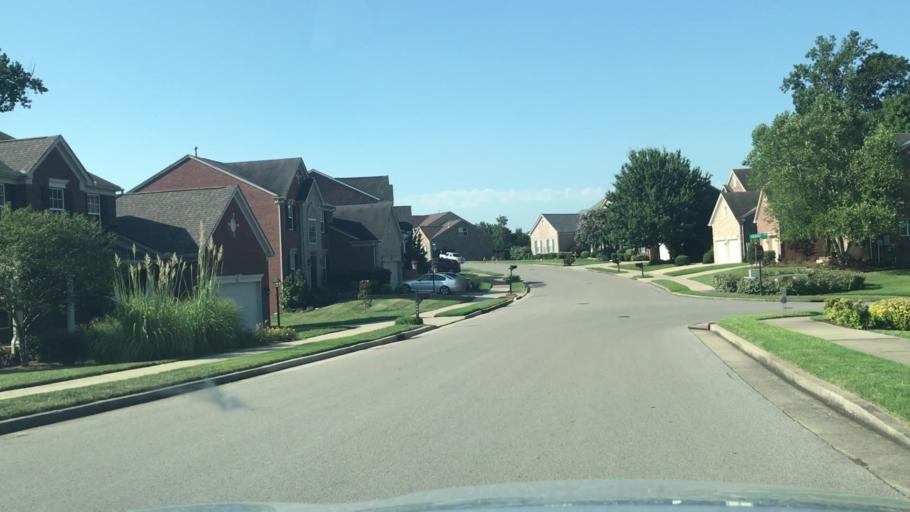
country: US
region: Tennessee
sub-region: Williamson County
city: Brentwood Estates
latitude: 36.0163
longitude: -86.7126
